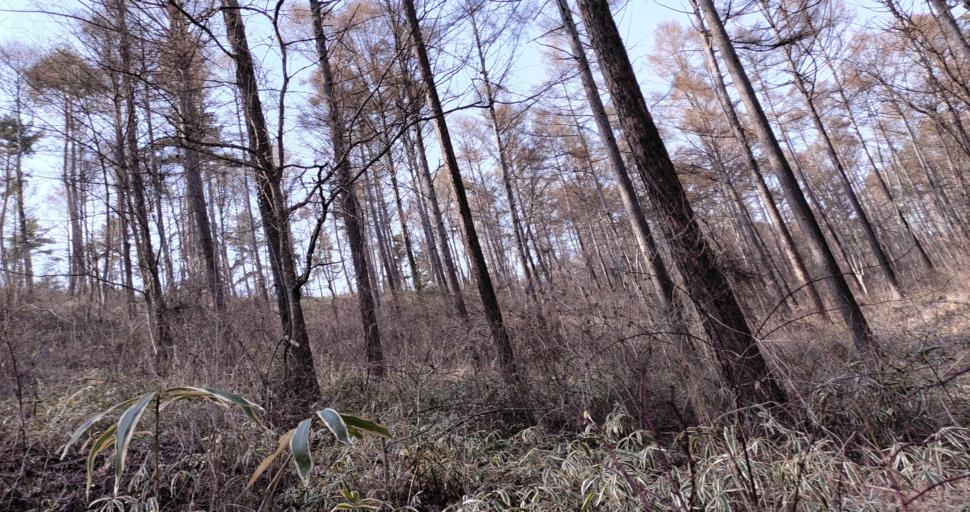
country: JP
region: Nagano
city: Komoro
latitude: 36.3690
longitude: 138.4525
